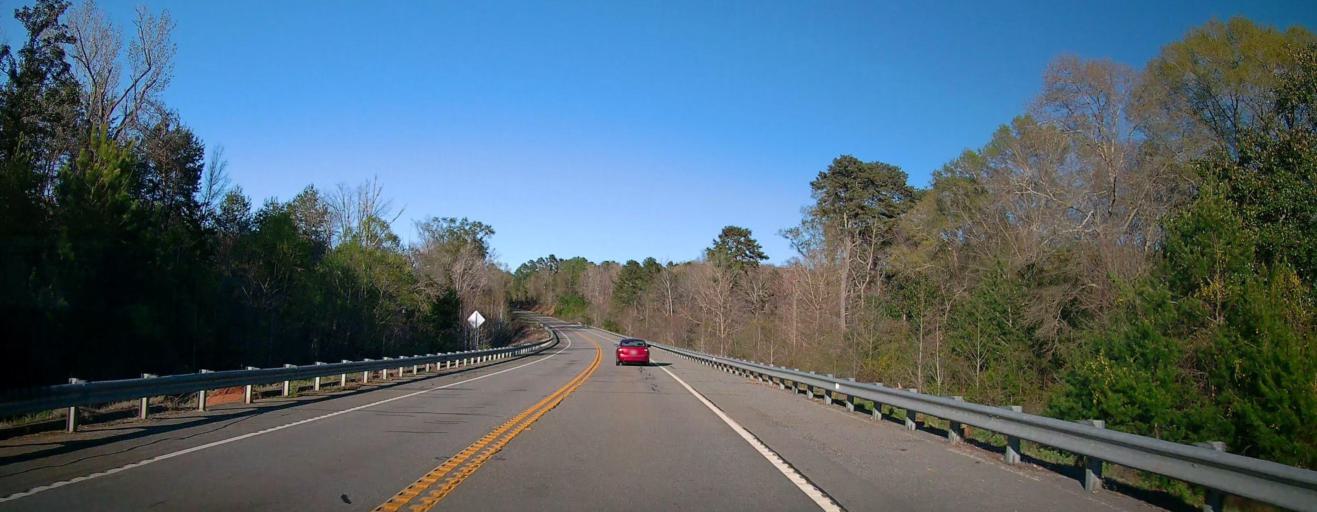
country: US
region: Georgia
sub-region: Pulaski County
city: Hawkinsville
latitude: 32.2626
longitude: -83.5610
